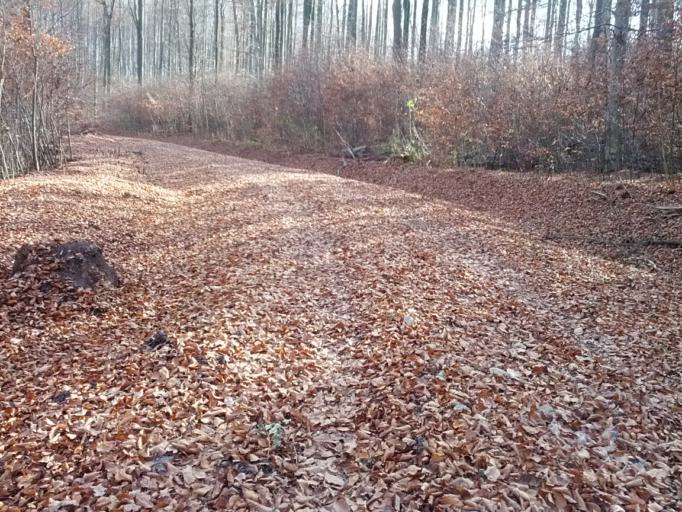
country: DE
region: Thuringia
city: Krauthausen
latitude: 50.9750
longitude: 10.2365
